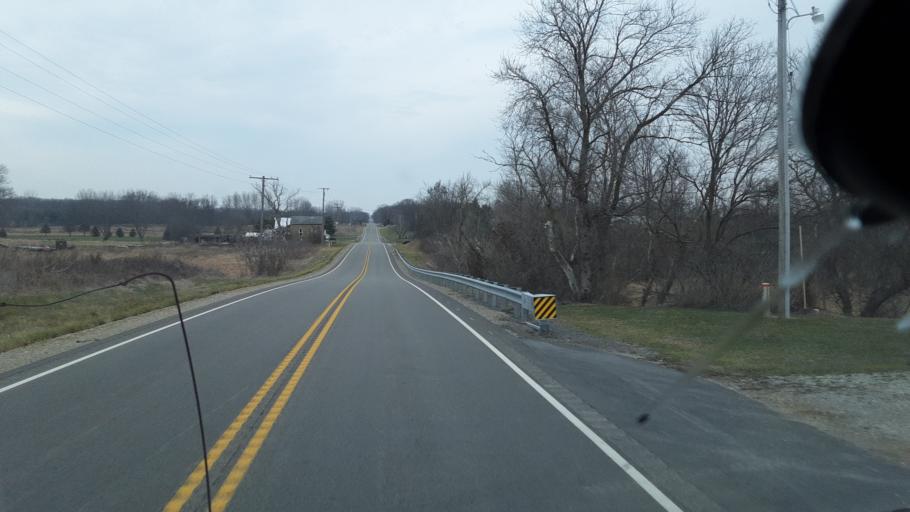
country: US
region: Indiana
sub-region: Noble County
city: Kendallville
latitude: 41.5614
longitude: -85.1684
